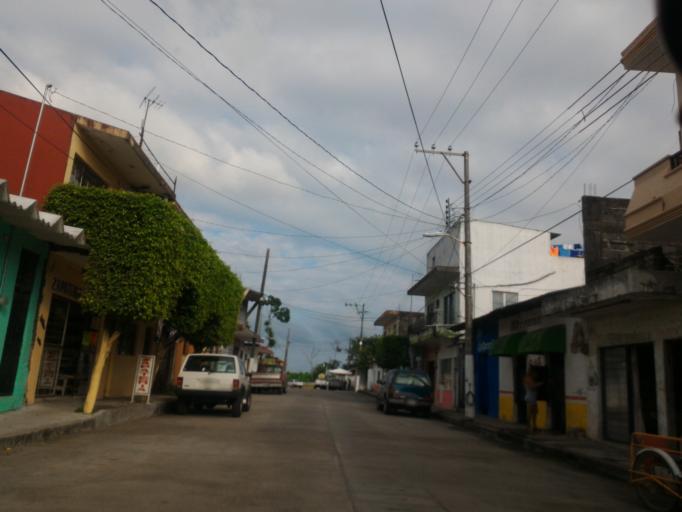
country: MX
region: Veracruz
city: San Rafael
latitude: 20.1873
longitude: -96.8656
